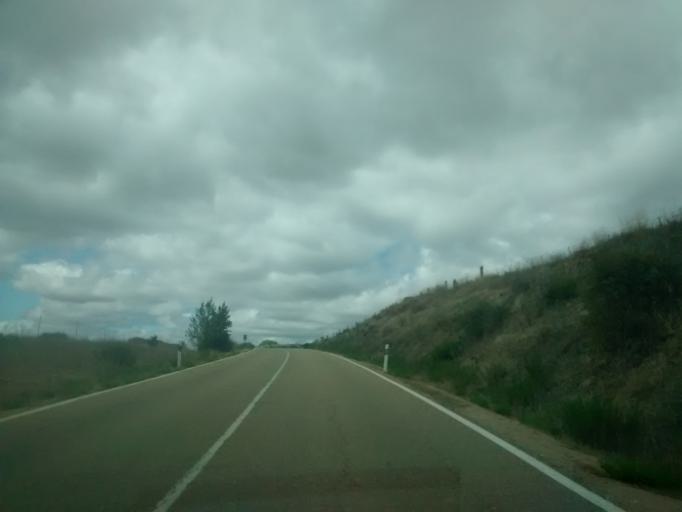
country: ES
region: Castille and Leon
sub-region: Provincia de Salamanca
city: Ciudad Rodrigo
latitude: 40.6233
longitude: -6.5056
